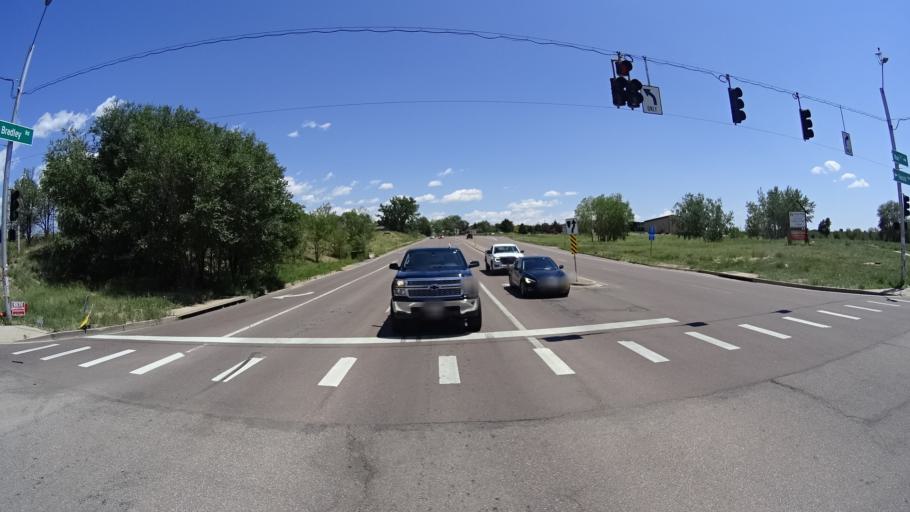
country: US
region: Colorado
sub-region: El Paso County
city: Security-Widefield
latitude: 38.7700
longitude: -104.7391
